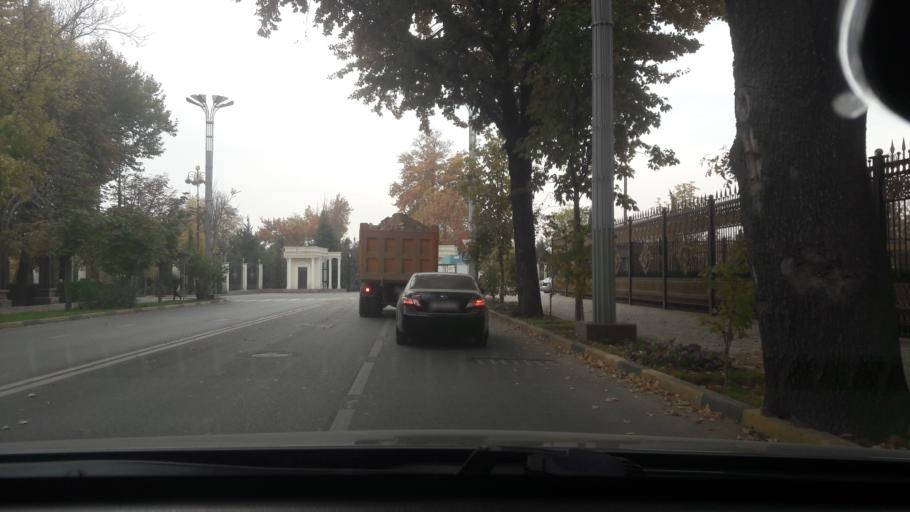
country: TJ
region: Dushanbe
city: Dushanbe
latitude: 38.5783
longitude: 68.7830
